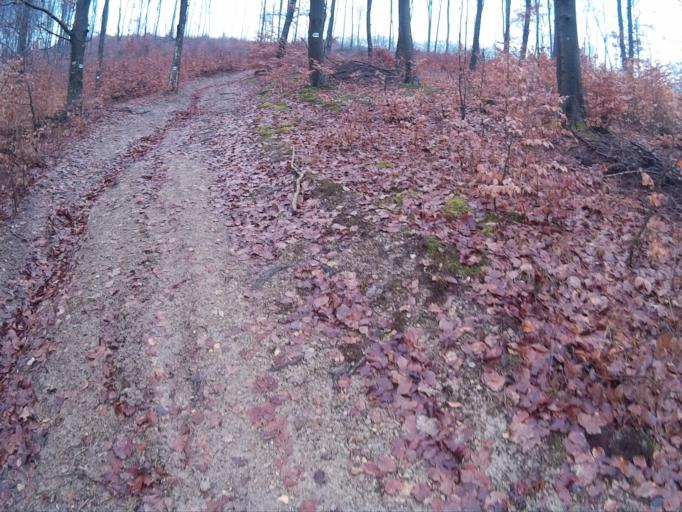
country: HU
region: Borsod-Abauj-Zemplen
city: Sarospatak
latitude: 48.4193
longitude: 21.5561
